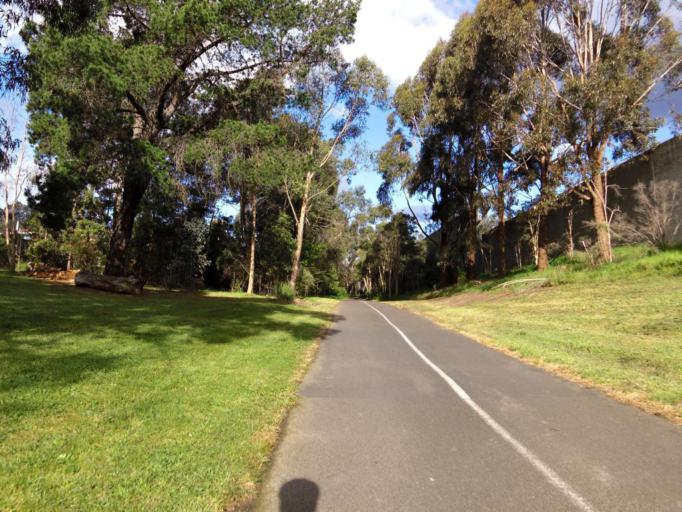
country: AU
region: Victoria
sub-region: Manningham
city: Doncaster East
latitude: -37.7989
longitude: 145.1464
